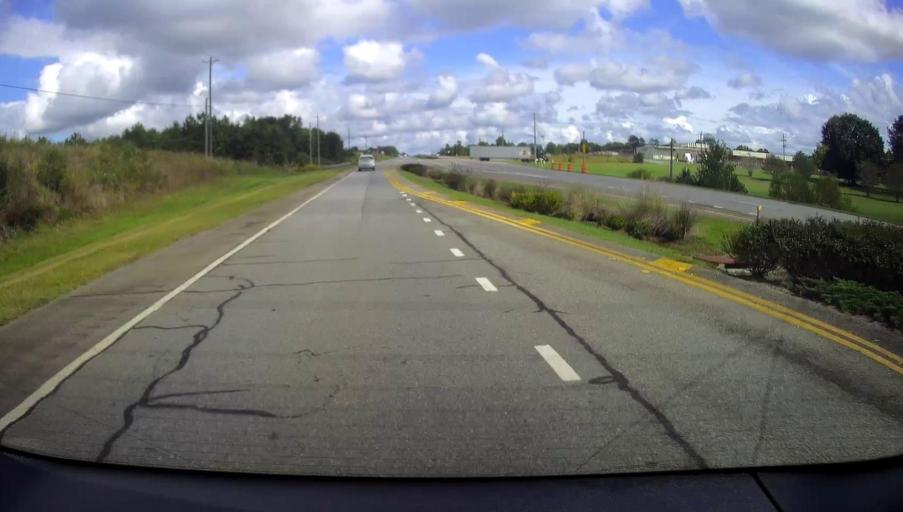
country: US
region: Georgia
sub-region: Baldwin County
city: Milledgeville
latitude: 33.0869
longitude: -83.2891
